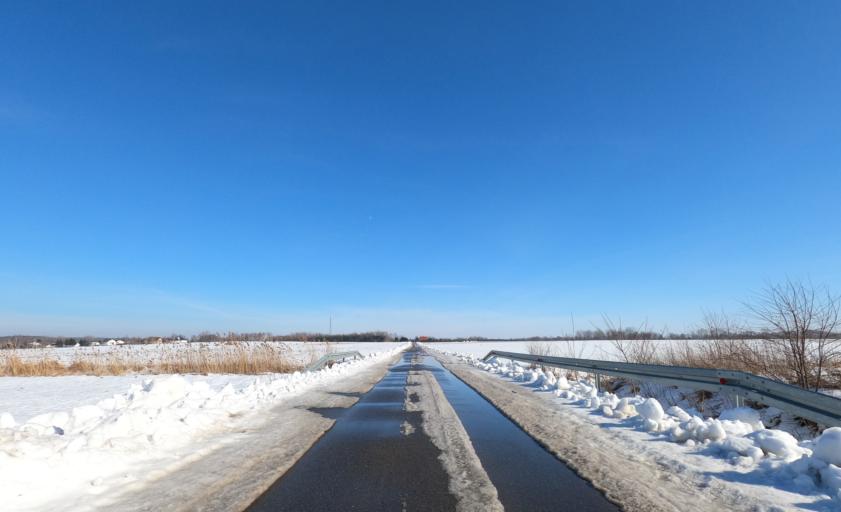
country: PL
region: Subcarpathian Voivodeship
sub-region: Powiat debicki
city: Brzeznica
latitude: 50.0836
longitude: 21.5026
